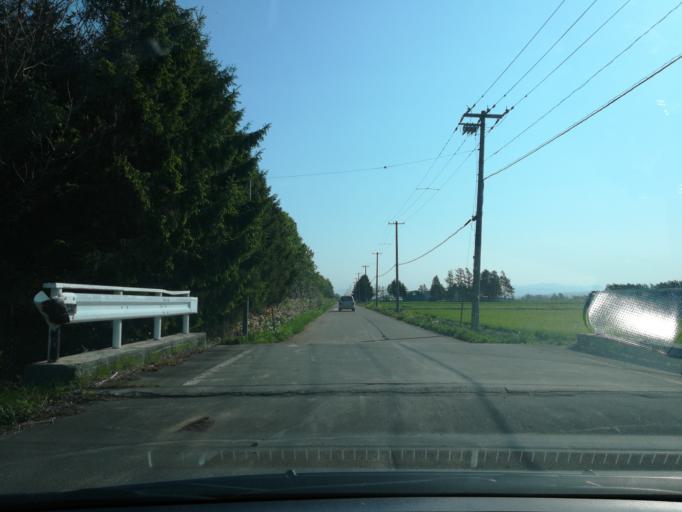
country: JP
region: Hokkaido
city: Ebetsu
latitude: 43.1221
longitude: 141.6589
